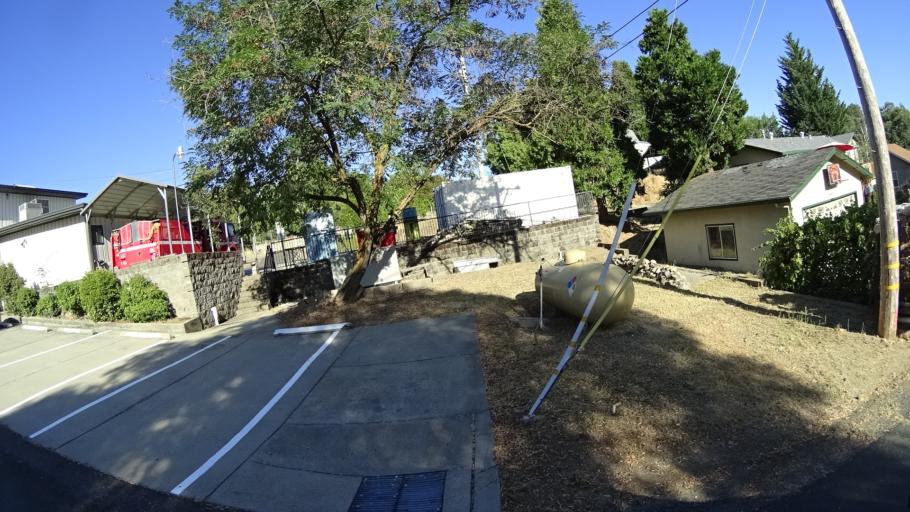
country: US
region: California
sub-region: Amador County
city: Jackson
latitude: 38.2990
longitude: -120.7030
